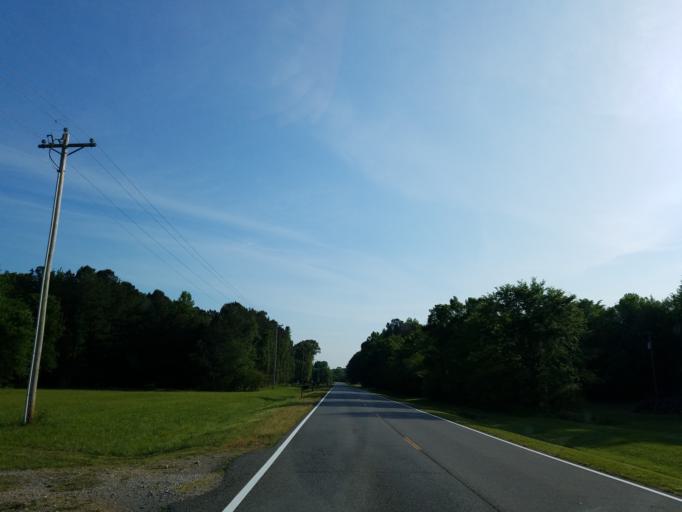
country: US
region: Georgia
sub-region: Chattooga County
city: Trion
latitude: 34.5469
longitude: -85.2004
